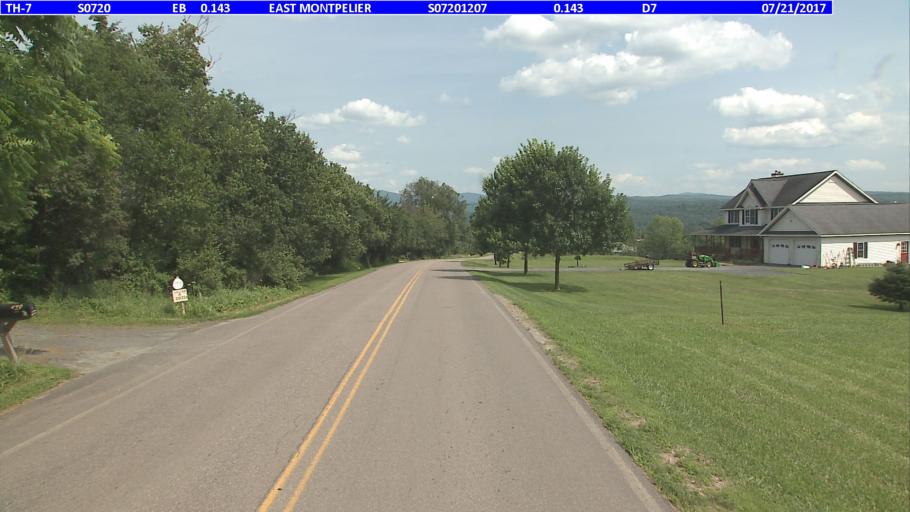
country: US
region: Vermont
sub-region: Washington County
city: Barre
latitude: 44.2764
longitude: -72.4972
